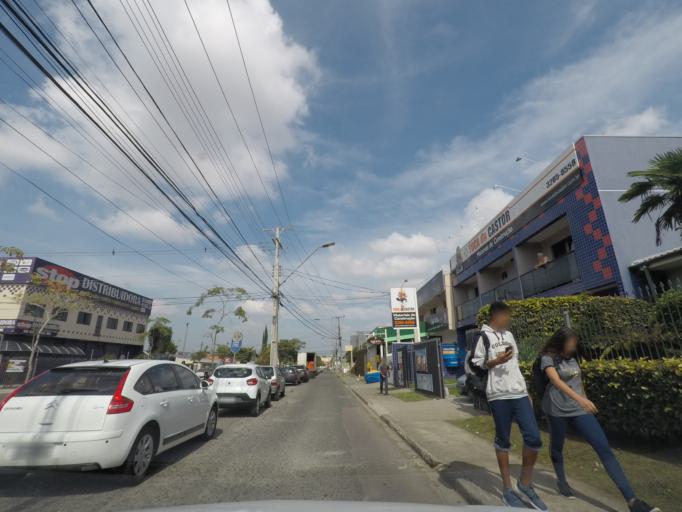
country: BR
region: Parana
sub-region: Pinhais
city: Pinhais
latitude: -25.4612
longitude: -49.2116
